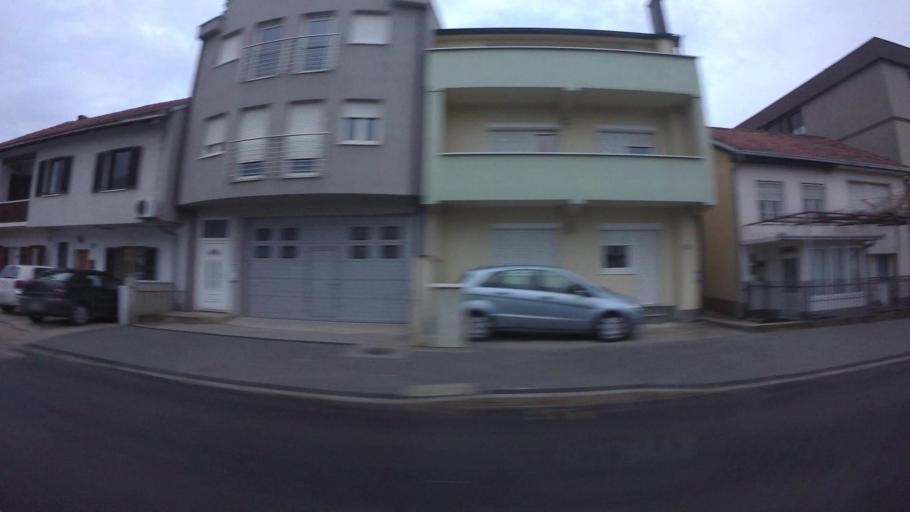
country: BA
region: Federation of Bosnia and Herzegovina
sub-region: Hercegovacko-Bosanski Kanton
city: Mostar
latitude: 43.3544
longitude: 17.8124
